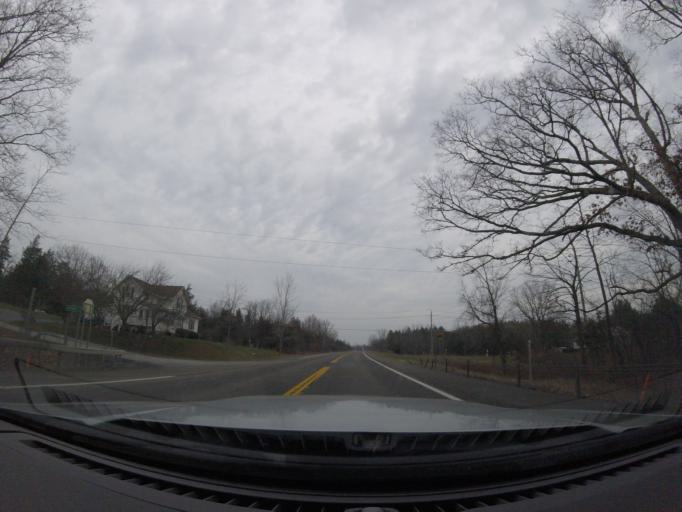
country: US
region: New York
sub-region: Yates County
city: Dundee
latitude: 42.5487
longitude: -76.9195
